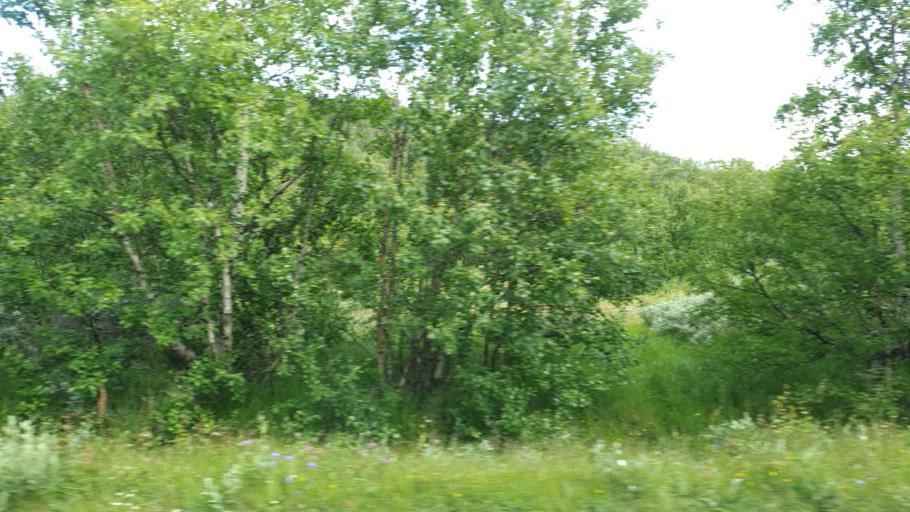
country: NO
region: Oppland
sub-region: Oystre Slidre
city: Heggenes
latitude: 61.4891
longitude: 8.8254
